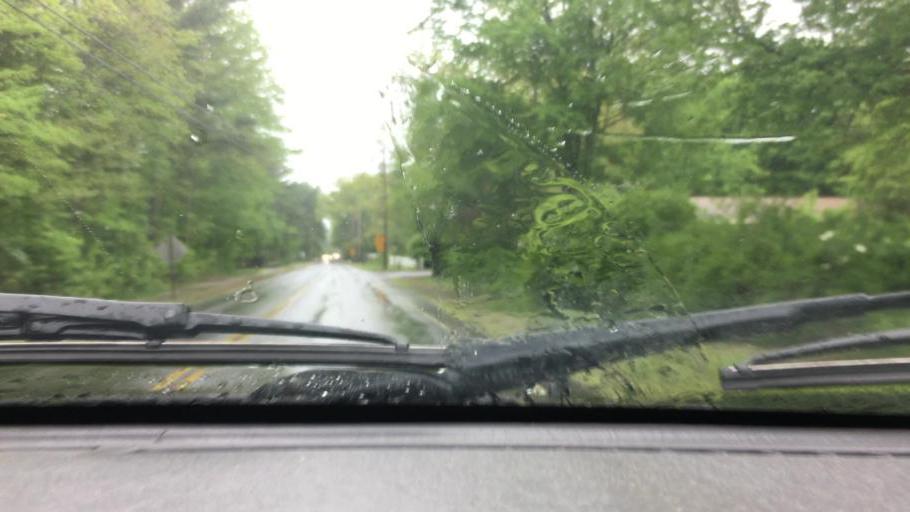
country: US
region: Massachusetts
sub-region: Franklin County
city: Turners Falls
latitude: 42.5887
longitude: -72.5504
